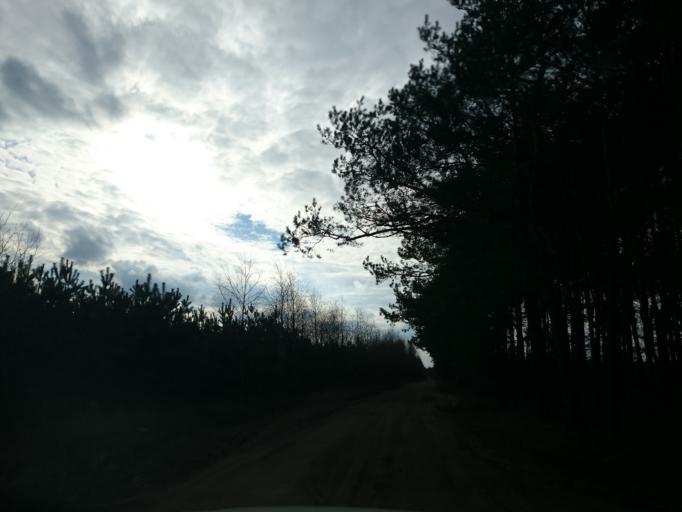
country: PL
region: Kujawsko-Pomorskie
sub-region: Powiat golubsko-dobrzynski
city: Ciechocin
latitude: 53.0503
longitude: 18.8547
